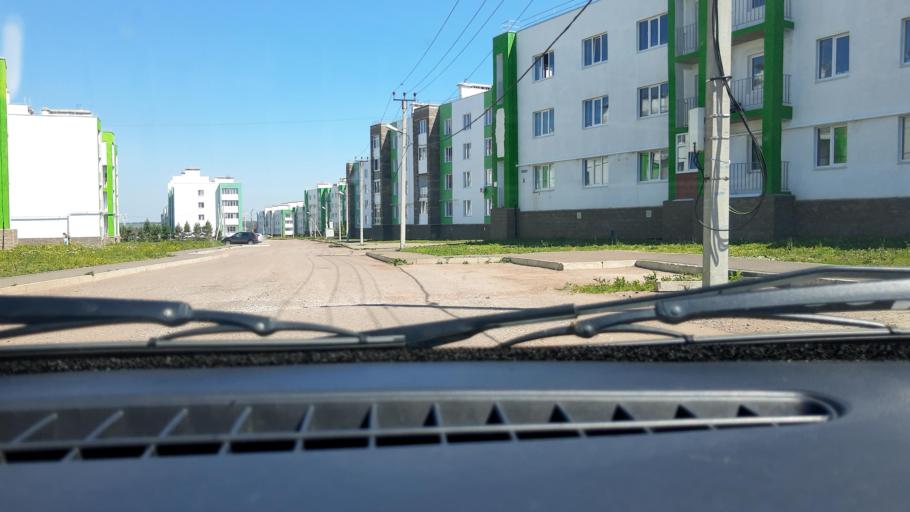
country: RU
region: Bashkortostan
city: Avdon
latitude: 54.4822
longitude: 55.8850
